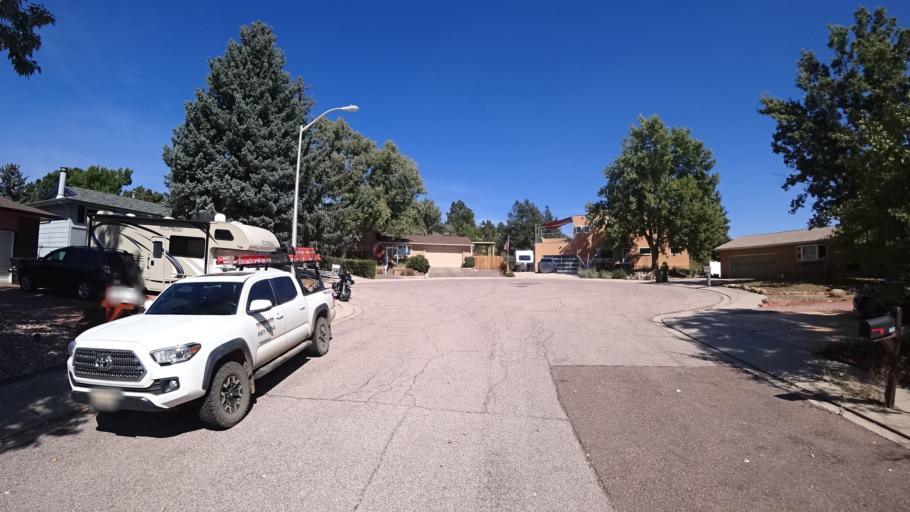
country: US
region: Colorado
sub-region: El Paso County
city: Cimarron Hills
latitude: 38.9108
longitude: -104.7642
